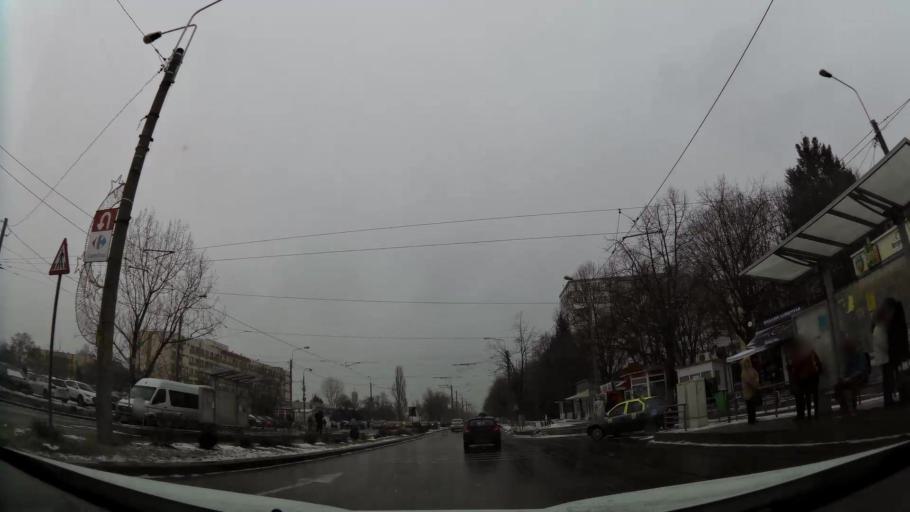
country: RO
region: Prahova
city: Ploiesti
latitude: 44.9631
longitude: 26.0072
